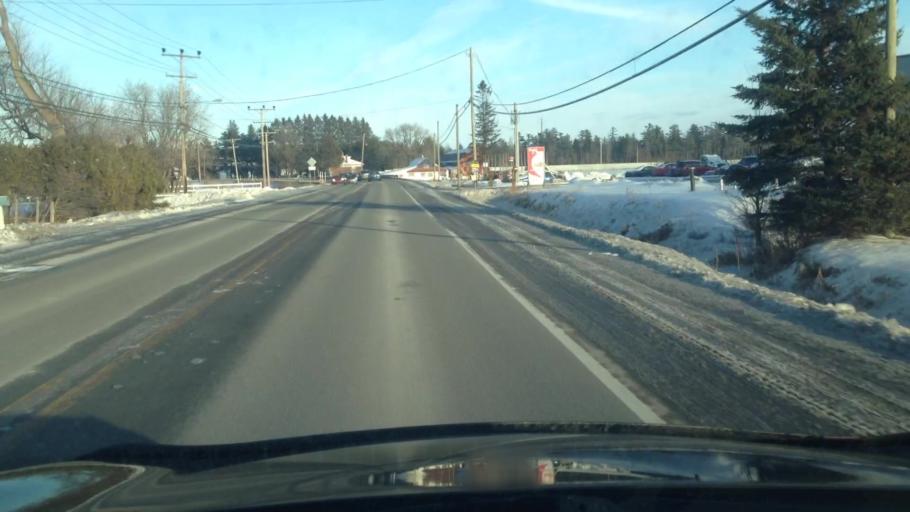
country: CA
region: Quebec
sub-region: Laurentides
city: Sainte-Sophie
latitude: 45.8110
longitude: -73.9191
